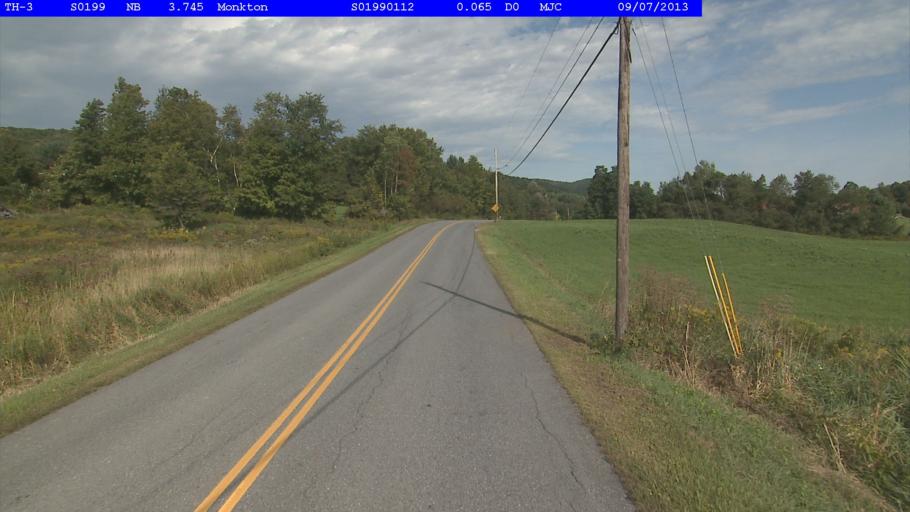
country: US
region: Vermont
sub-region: Addison County
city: Bristol
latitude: 44.1819
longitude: -73.1047
